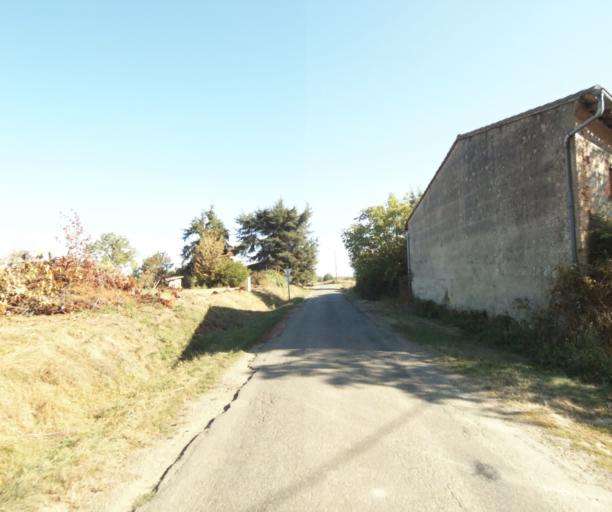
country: FR
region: Midi-Pyrenees
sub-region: Departement du Tarn-et-Garonne
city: Verdun-sur-Garonne
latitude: 43.8565
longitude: 1.2105
